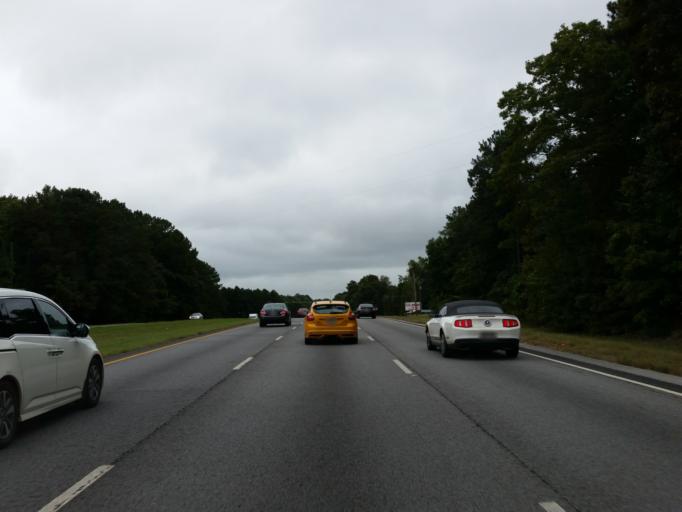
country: US
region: Georgia
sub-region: Henry County
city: Hampton
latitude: 33.3664
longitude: -84.2963
